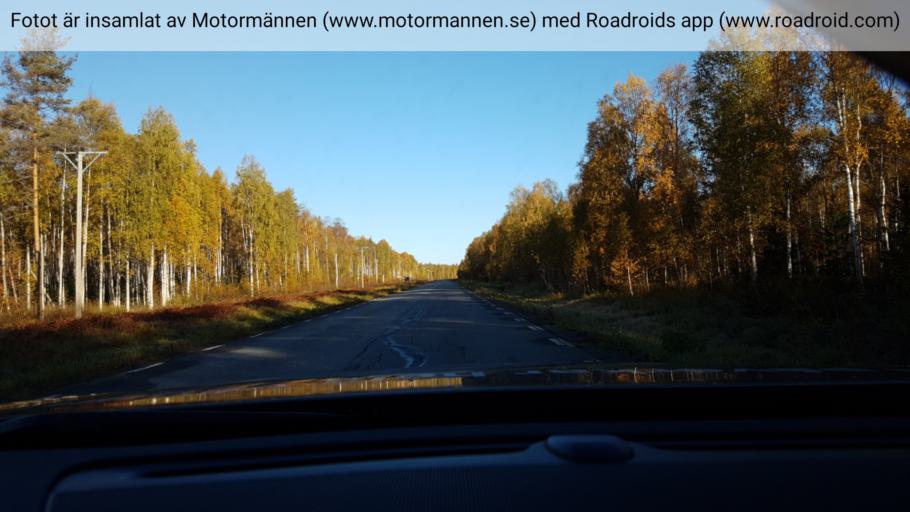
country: SE
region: Norrbotten
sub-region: Bodens Kommun
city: Boden
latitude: 65.9147
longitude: 21.6599
